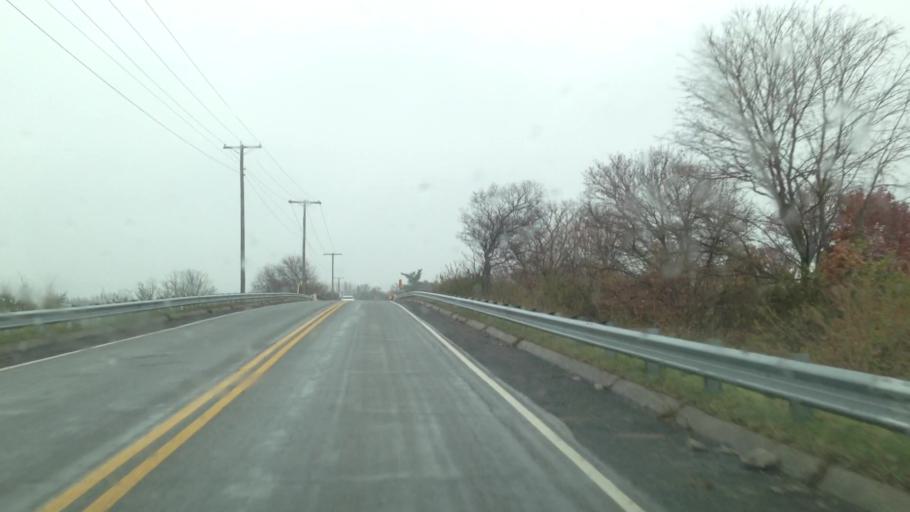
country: US
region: Indiana
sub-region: Saint Joseph County
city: Mishawaka
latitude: 41.7179
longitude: -86.1634
